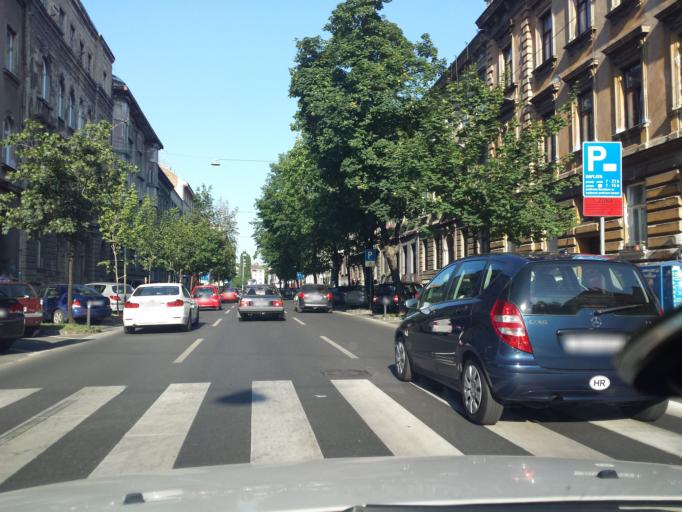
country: HR
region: Grad Zagreb
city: Zagreb - Centar
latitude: 45.8077
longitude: 15.9820
